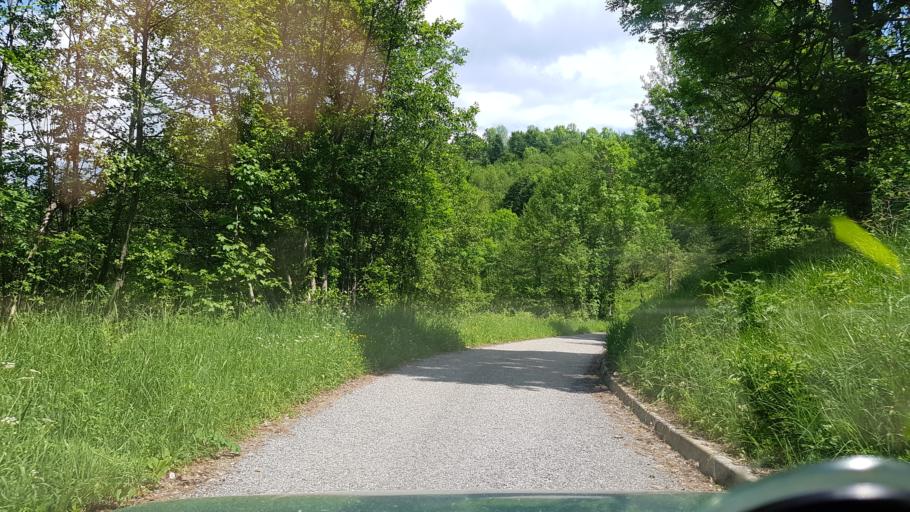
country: IT
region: Friuli Venezia Giulia
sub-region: Provincia di Udine
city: Pulfero
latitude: 46.1974
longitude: 13.4298
